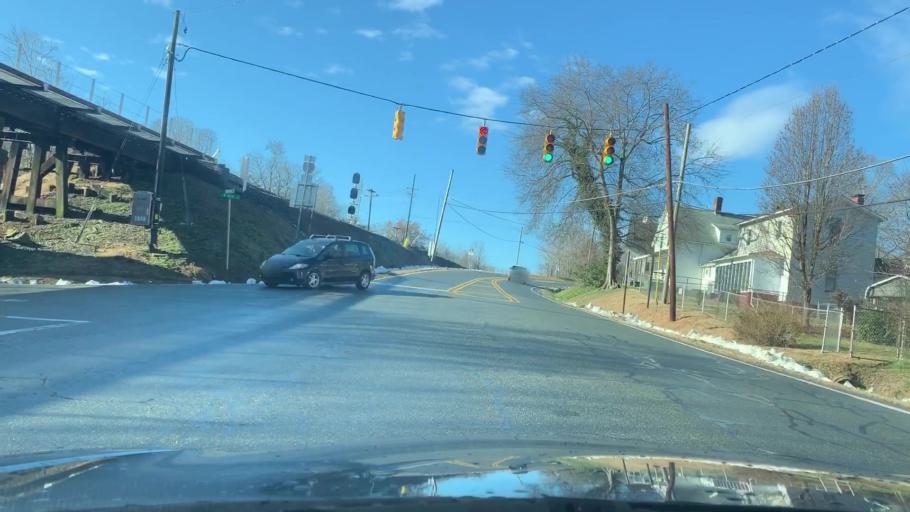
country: US
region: North Carolina
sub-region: Alamance County
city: Haw River
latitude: 36.0879
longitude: -79.3703
